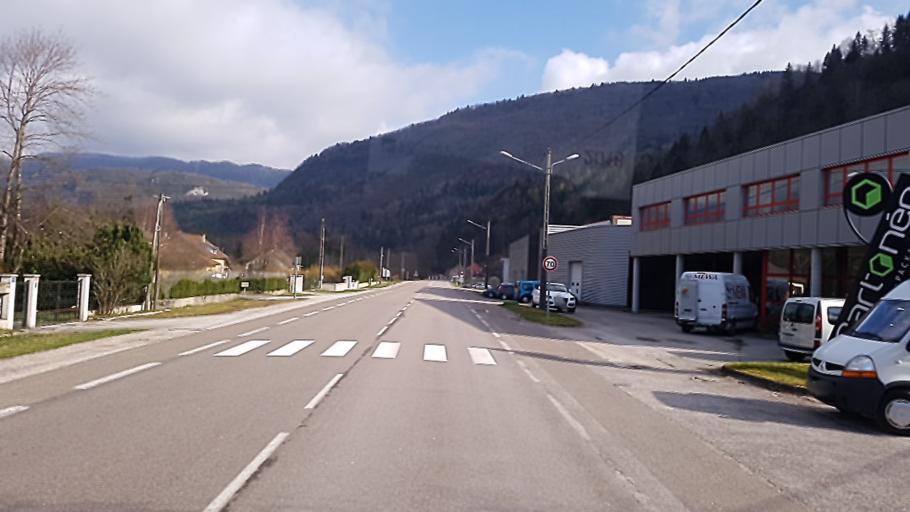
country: FR
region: Franche-Comte
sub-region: Departement du Jura
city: Lavans-les-Saint-Claude
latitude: 46.3538
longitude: 5.7424
